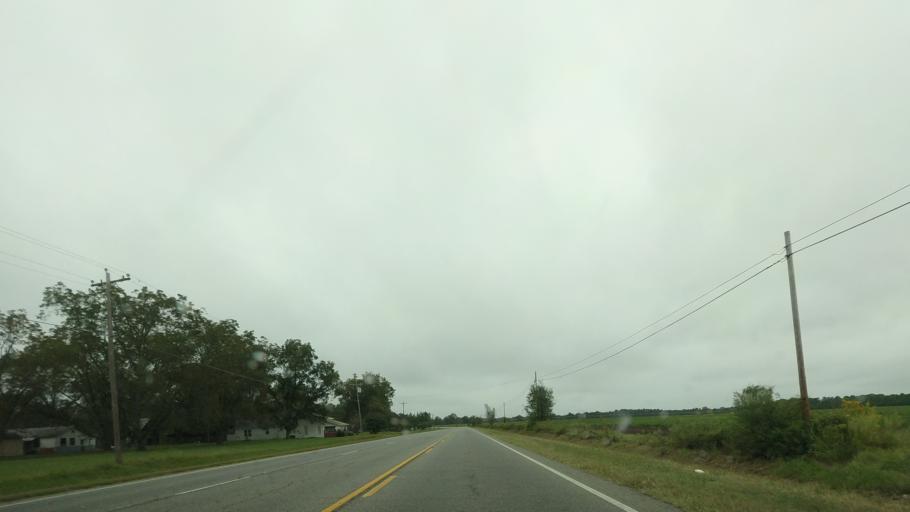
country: US
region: Georgia
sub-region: Ben Hill County
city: Fitzgerald
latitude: 31.6607
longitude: -83.2381
